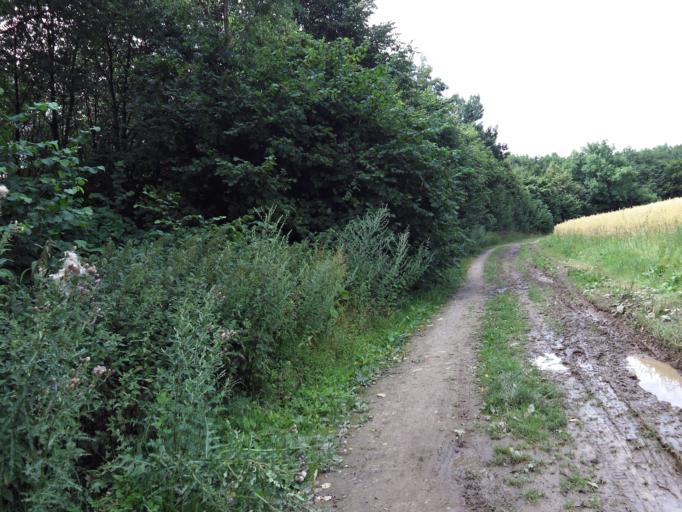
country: NL
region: Limburg
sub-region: Gemeente Schinnen
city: Doenrade
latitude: 50.9805
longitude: 5.8875
